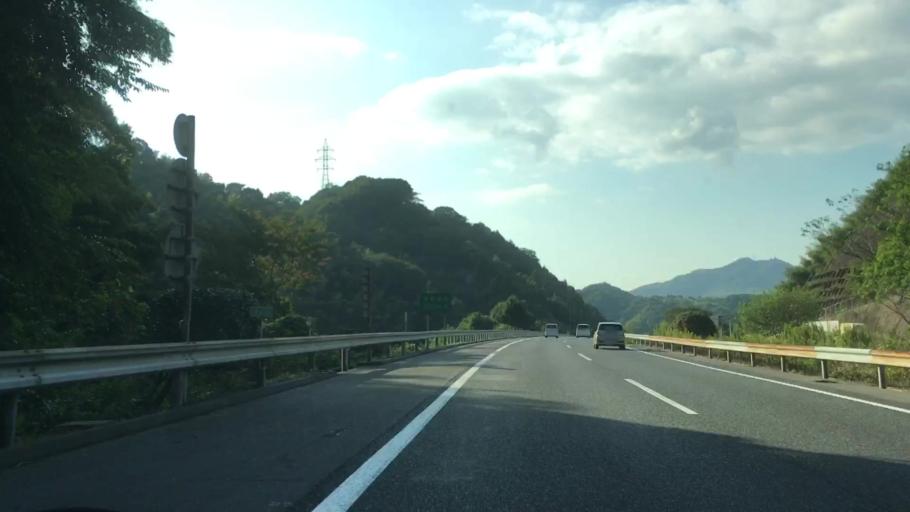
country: JP
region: Yamaguchi
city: Tokuyama
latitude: 34.0737
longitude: 131.8069
